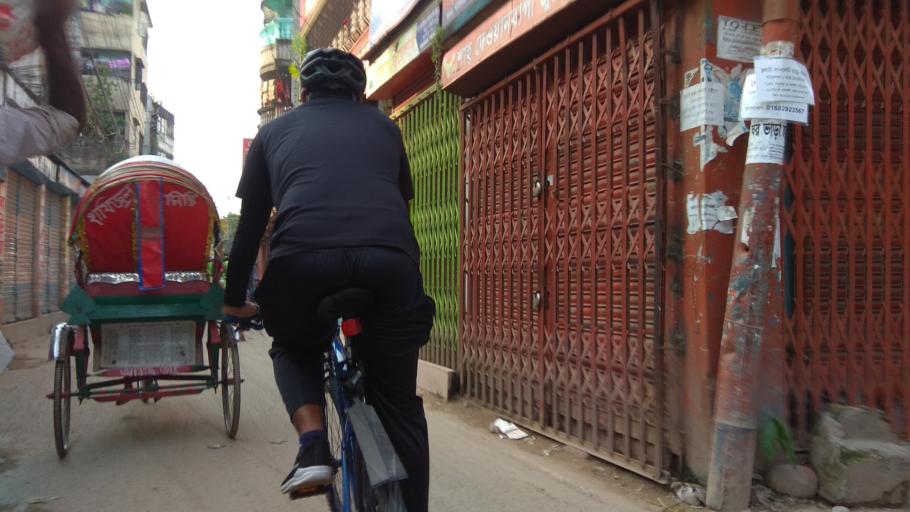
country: BD
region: Dhaka
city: Tungi
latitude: 23.8263
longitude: 90.3937
